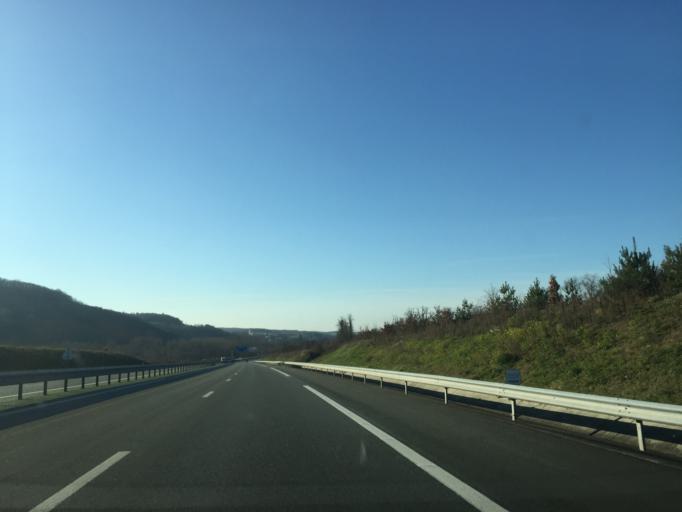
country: FR
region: Aquitaine
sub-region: Departement de la Dordogne
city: Montignac
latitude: 45.1483
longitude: 1.1863
